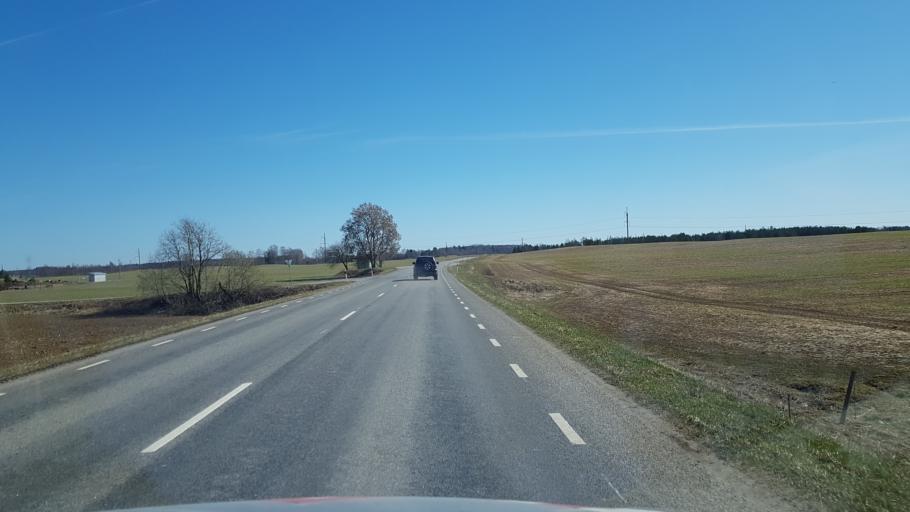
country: EE
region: Laeaene-Virumaa
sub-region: Vinni vald
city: Vinni
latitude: 59.3227
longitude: 26.4315
